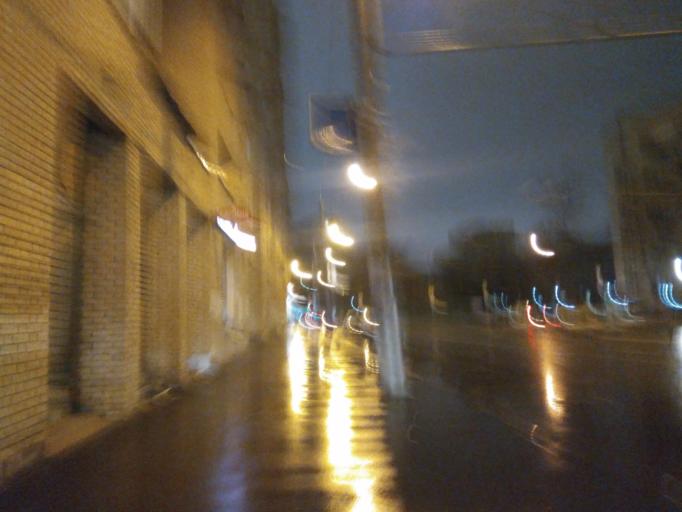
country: RU
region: Moscow
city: Moscow
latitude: 55.7751
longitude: 37.5927
